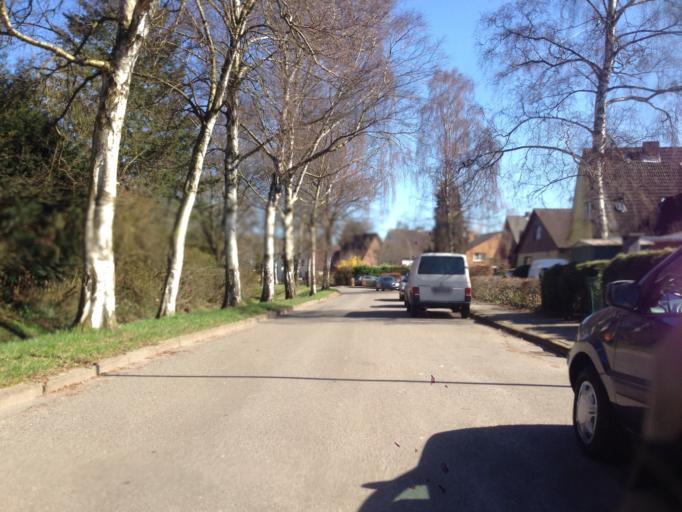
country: DE
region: Hamburg
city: Steilshoop
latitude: 53.5977
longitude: 10.0864
